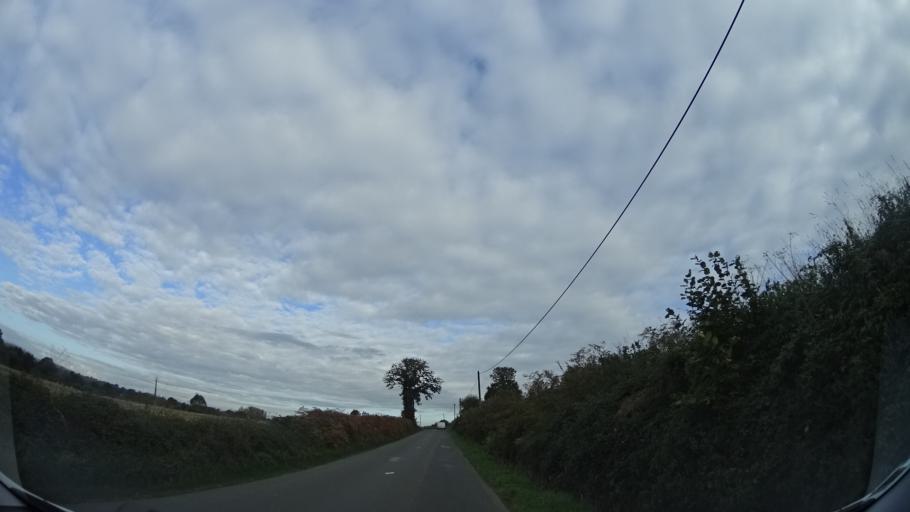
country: FR
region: Brittany
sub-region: Departement d'Ille-et-Vilaine
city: Geveze
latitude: 48.2302
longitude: -1.7865
